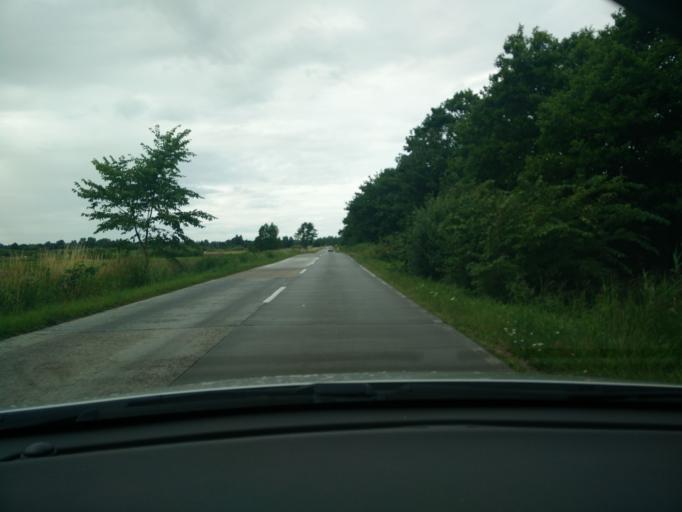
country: PL
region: Pomeranian Voivodeship
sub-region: Powiat pucki
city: Mrzezino
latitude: 54.6164
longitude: 18.4475
